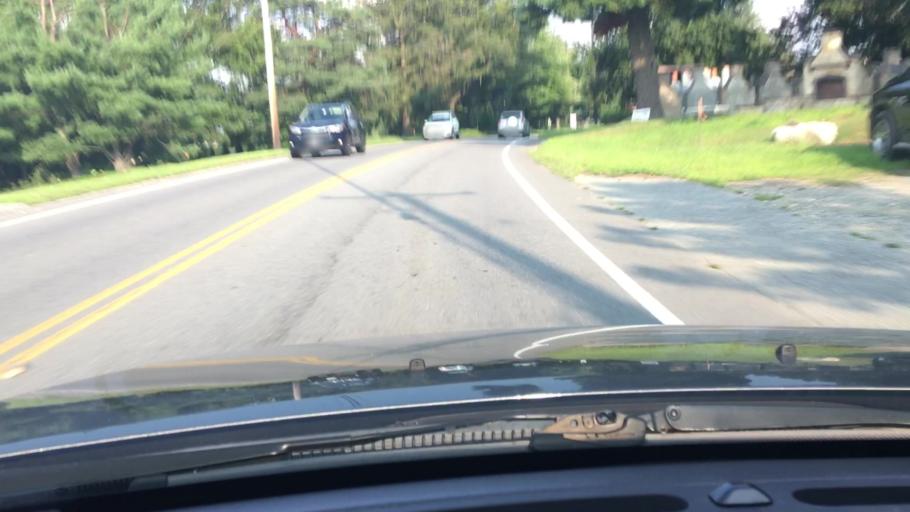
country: US
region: Massachusetts
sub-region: Worcester County
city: Westborough
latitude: 42.2569
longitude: -71.5951
